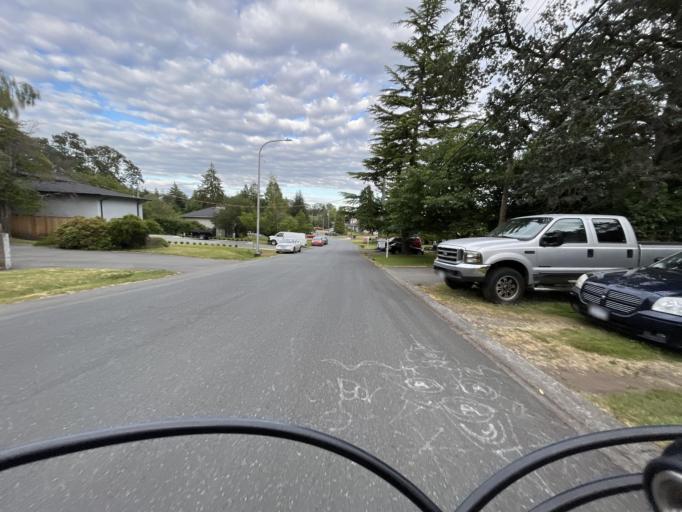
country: CA
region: British Columbia
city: Oak Bay
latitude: 48.4799
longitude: -123.3387
